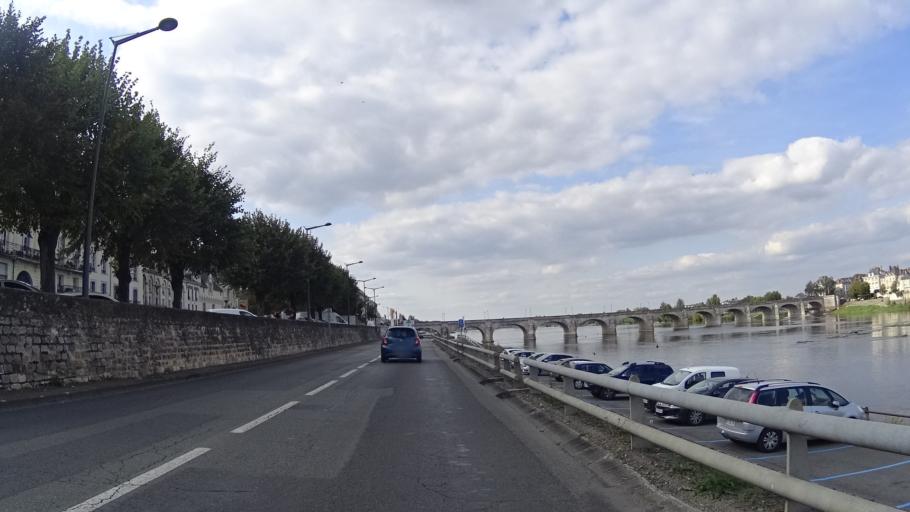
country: FR
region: Pays de la Loire
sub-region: Departement de Maine-et-Loire
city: Saumur
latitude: 47.2596
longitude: -0.0734
